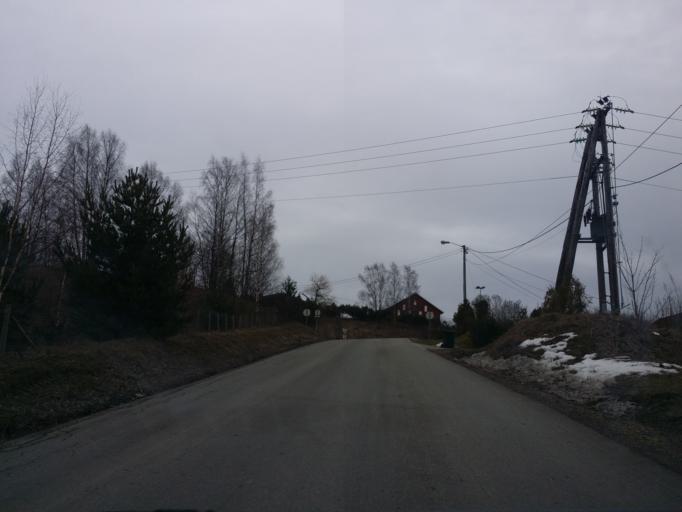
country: NO
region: Buskerud
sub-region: Lier
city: Tranby
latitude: 59.8161
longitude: 10.2464
